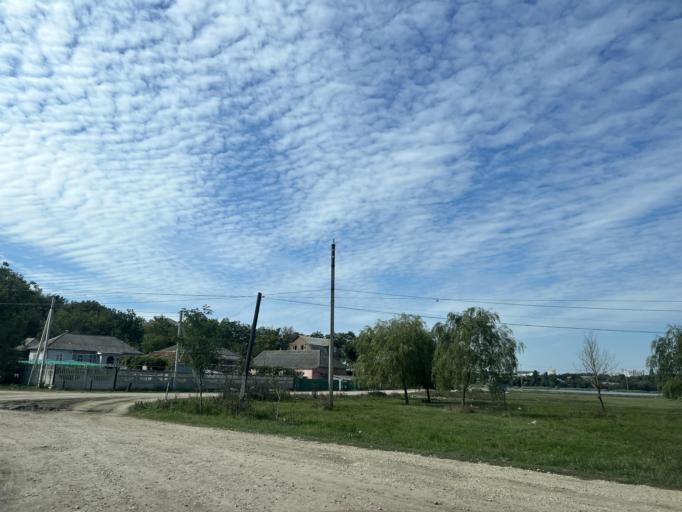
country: MD
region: Ungheni
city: Ungheni
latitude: 47.1973
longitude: 27.8112
